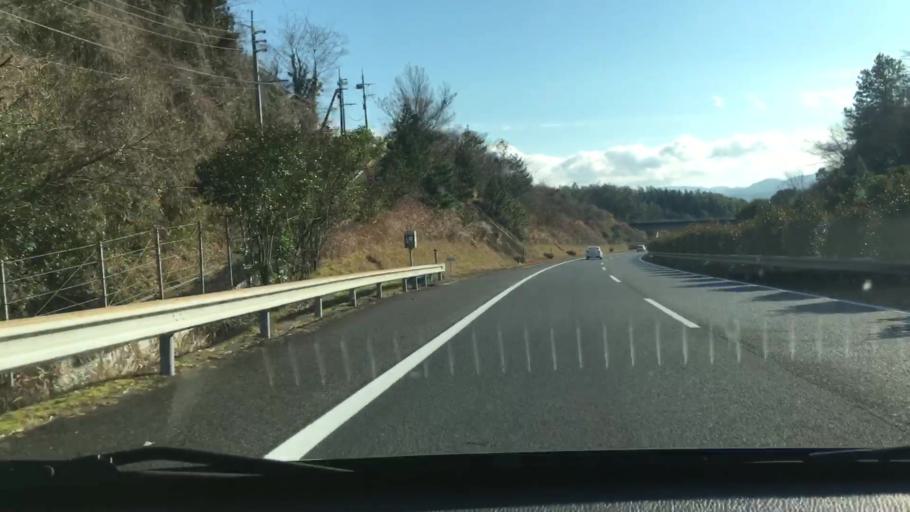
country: JP
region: Kumamoto
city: Hitoyoshi
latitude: 32.2209
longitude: 130.7802
